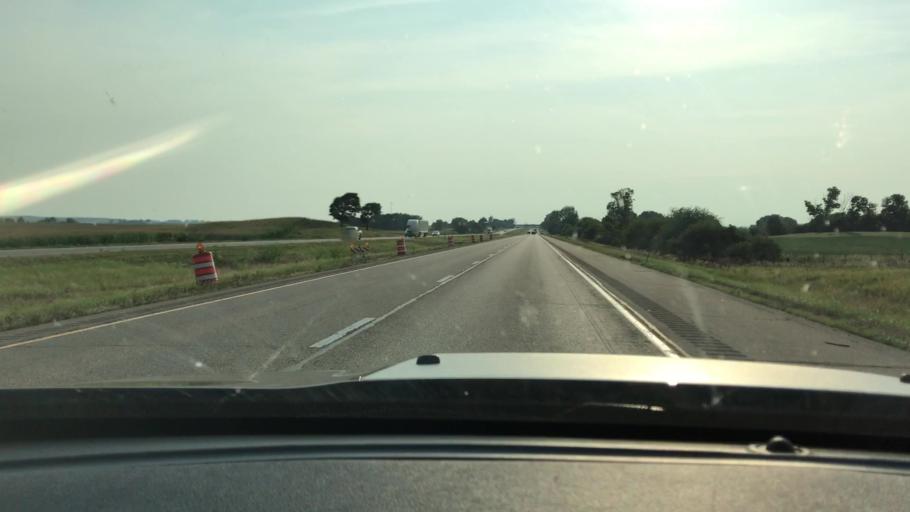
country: US
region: Illinois
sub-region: Henry County
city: Kewanee
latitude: 41.3874
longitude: -89.7482
